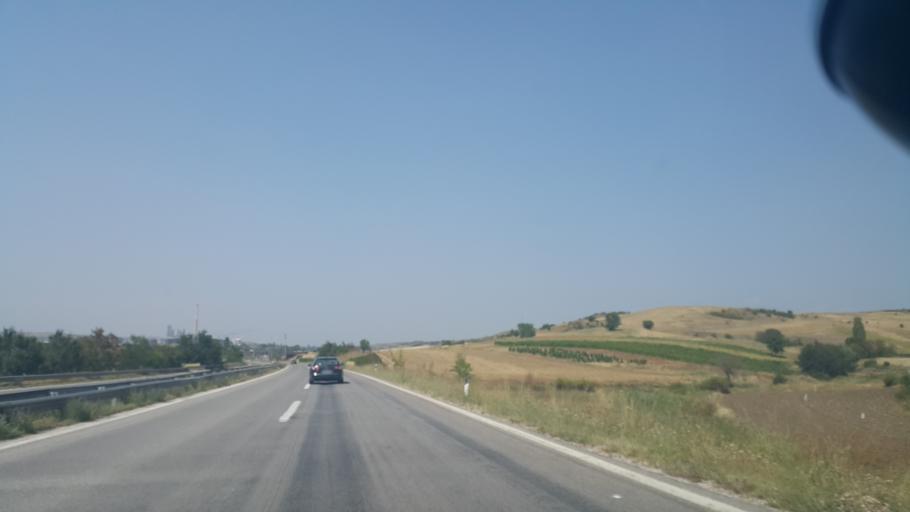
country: MK
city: Miladinovci
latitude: 41.9786
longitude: 21.6520
